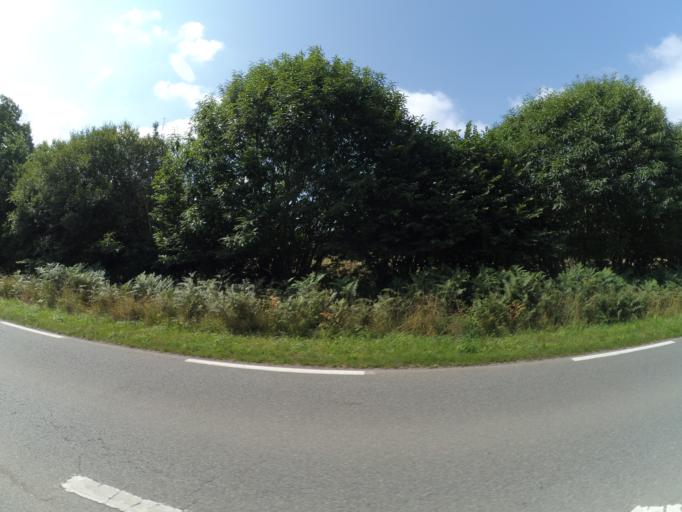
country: FR
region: Brittany
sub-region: Departement du Finistere
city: Rosporden
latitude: 47.9524
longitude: -3.7904
